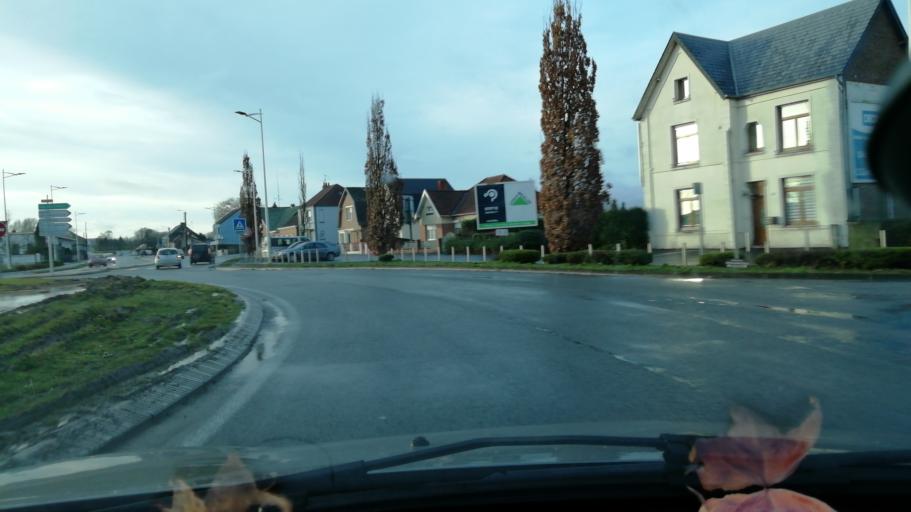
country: FR
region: Nord-Pas-de-Calais
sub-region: Departement du Nord
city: Feignies
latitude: 50.2803
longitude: 3.9235
